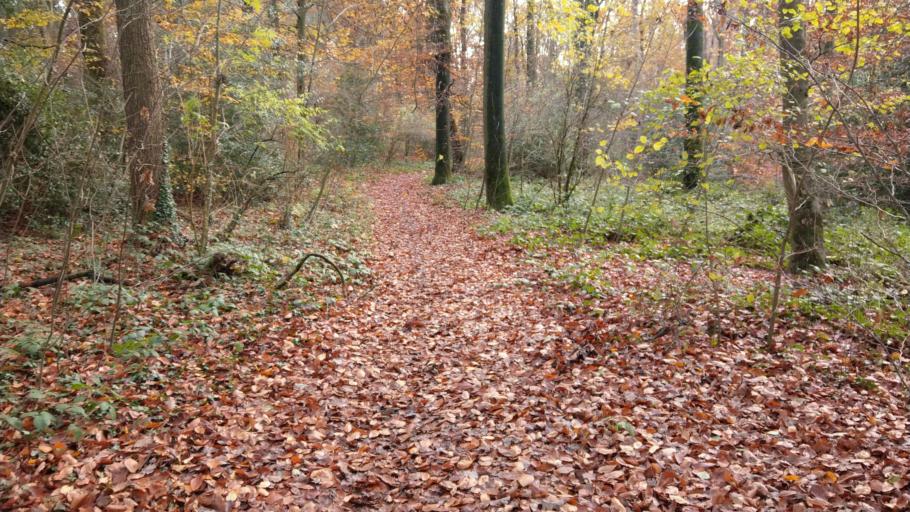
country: DE
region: North Rhine-Westphalia
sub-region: Regierungsbezirk Koln
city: Aachen
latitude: 50.7361
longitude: 6.0842
